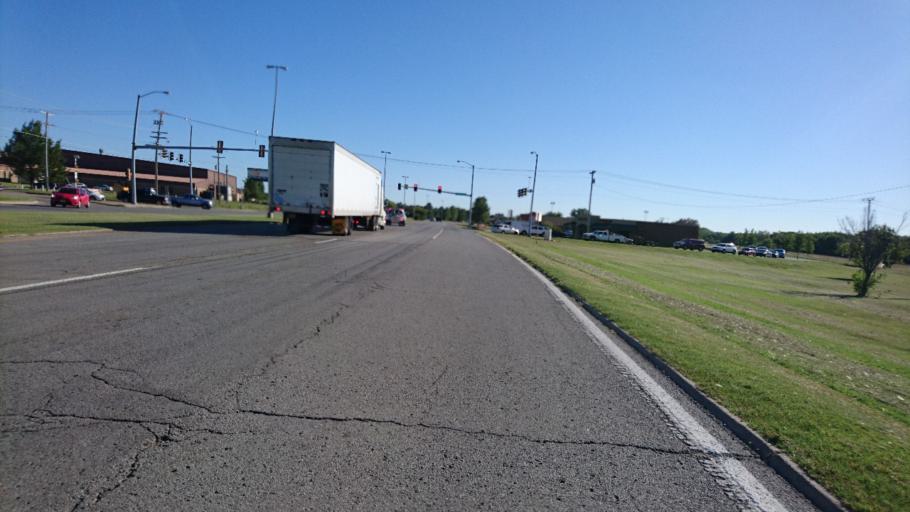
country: US
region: Oklahoma
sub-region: Rogers County
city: Claremore
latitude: 36.3299
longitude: -95.6061
